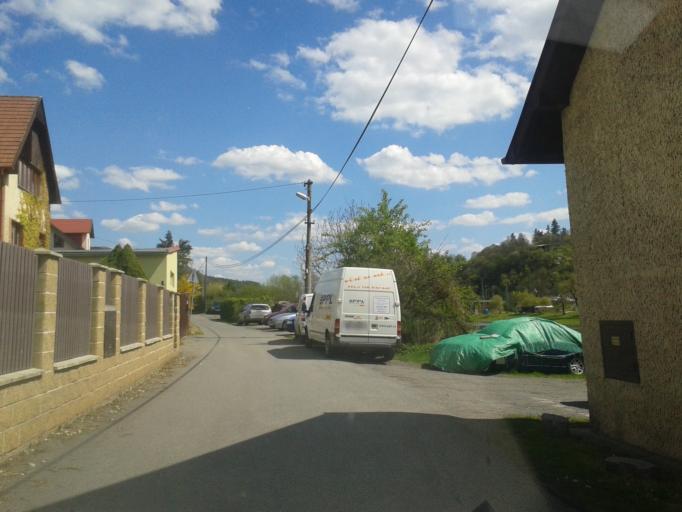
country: CZ
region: Central Bohemia
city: Nizbor
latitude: 50.0026
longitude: 13.9989
